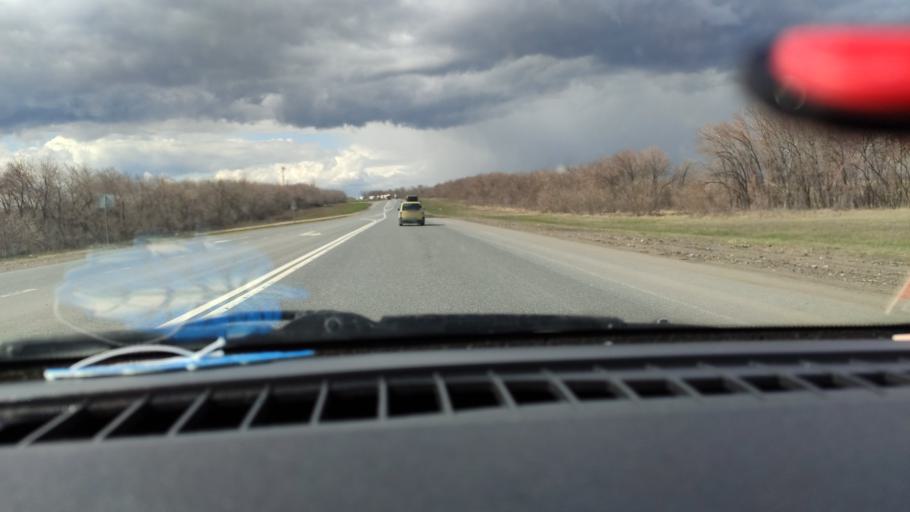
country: RU
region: Samara
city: Mezhdurechensk
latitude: 53.2556
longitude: 49.1369
